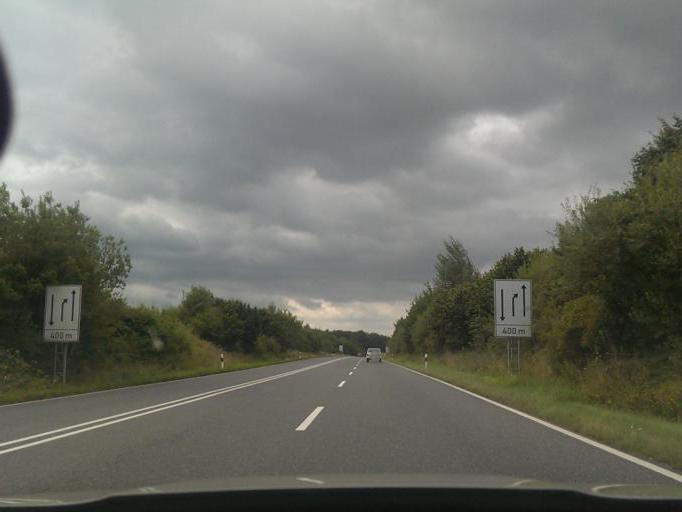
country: DE
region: Lower Saxony
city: Bevern
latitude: 51.8631
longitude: 9.5270
